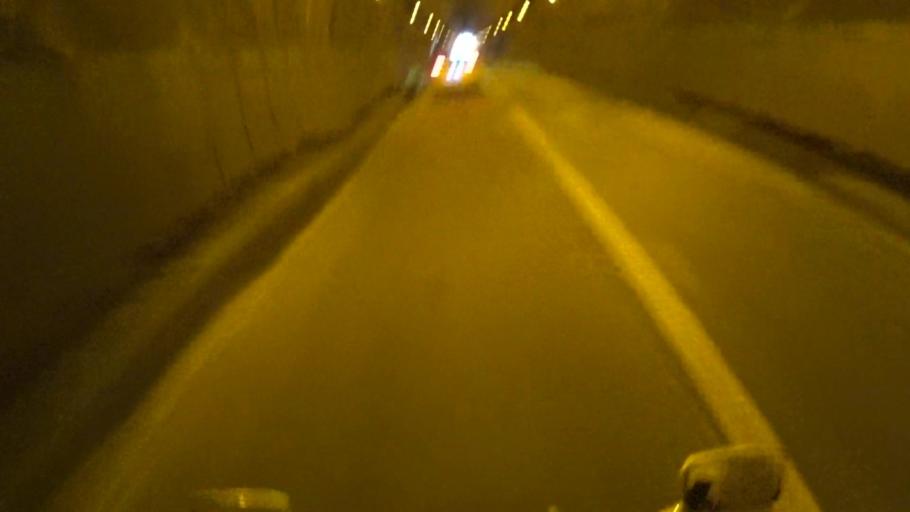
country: JP
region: Kyoto
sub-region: Kyoto-shi
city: Kamigyo-ku
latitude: 35.1155
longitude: 135.6630
